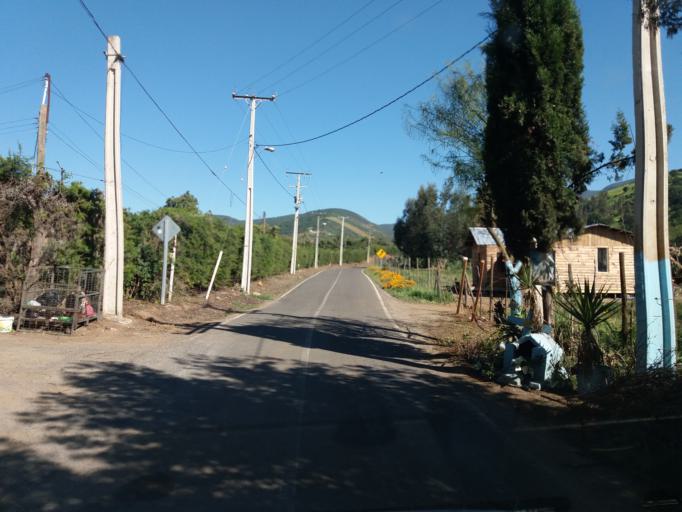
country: CL
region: Valparaiso
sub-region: Provincia de Quillota
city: Quillota
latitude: -32.8641
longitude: -71.2754
